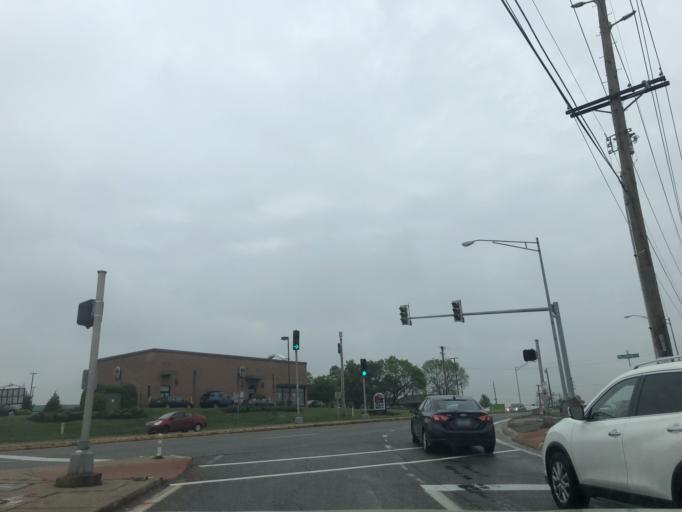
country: US
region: Missouri
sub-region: Saint Louis County
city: Shrewsbury
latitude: 38.5831
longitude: -90.3179
